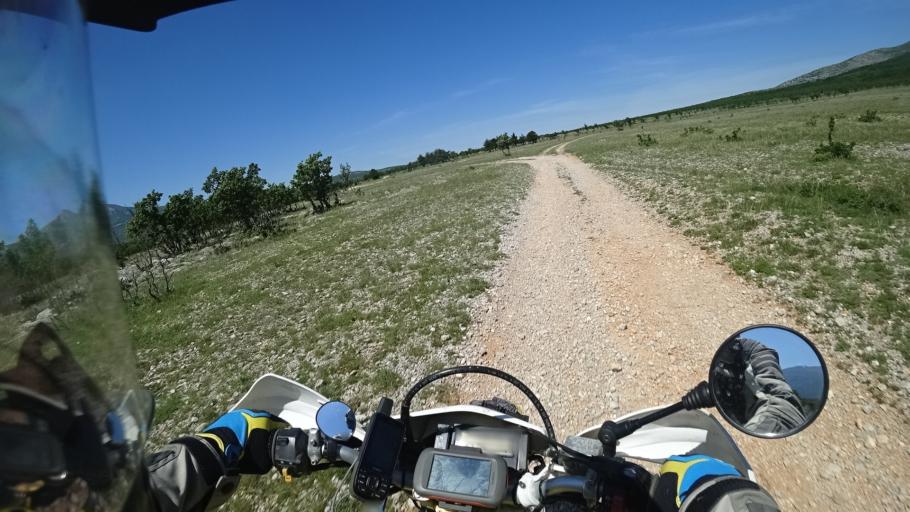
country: BA
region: Federation of Bosnia and Herzegovina
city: Bosansko Grahovo
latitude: 44.0047
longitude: 16.3923
